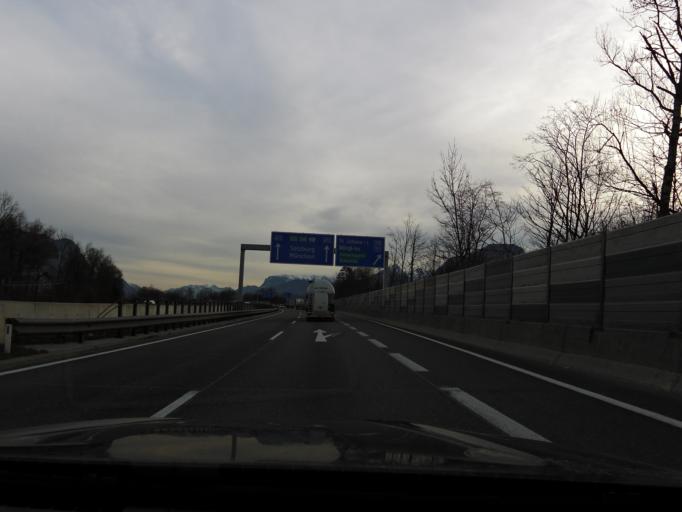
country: AT
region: Tyrol
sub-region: Politischer Bezirk Kufstein
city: Worgl
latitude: 47.4910
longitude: 12.0535
